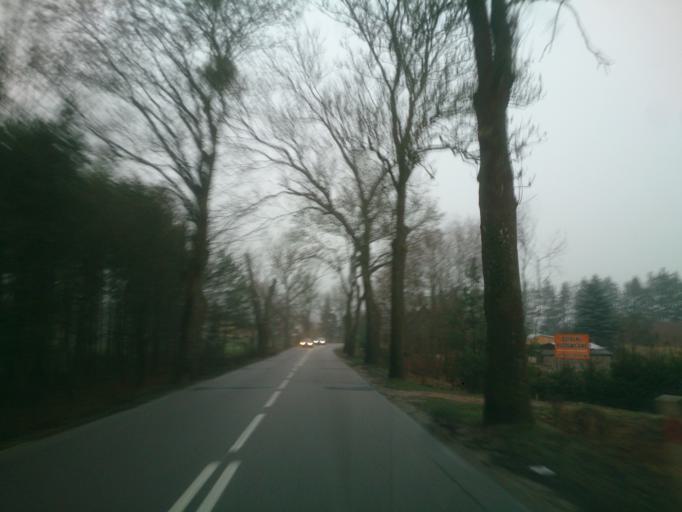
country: PL
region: Pomeranian Voivodeship
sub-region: Powiat starogardzki
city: Zblewo
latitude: 53.8957
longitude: 18.3486
